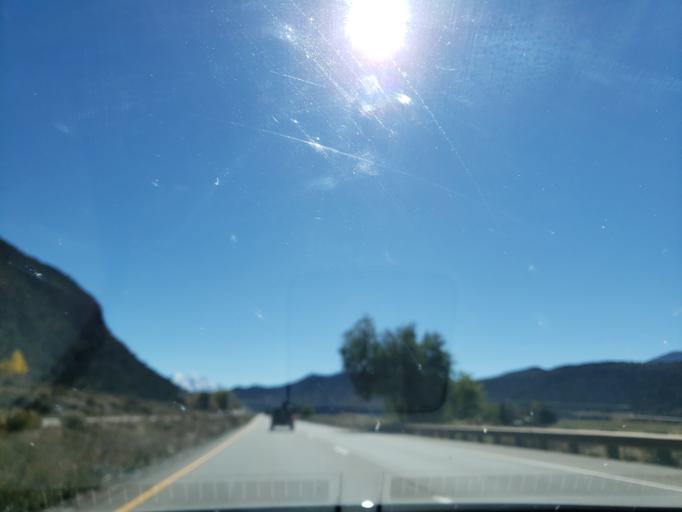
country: US
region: Colorado
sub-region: Garfield County
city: Glenwood Springs
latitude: 39.4966
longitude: -107.3009
